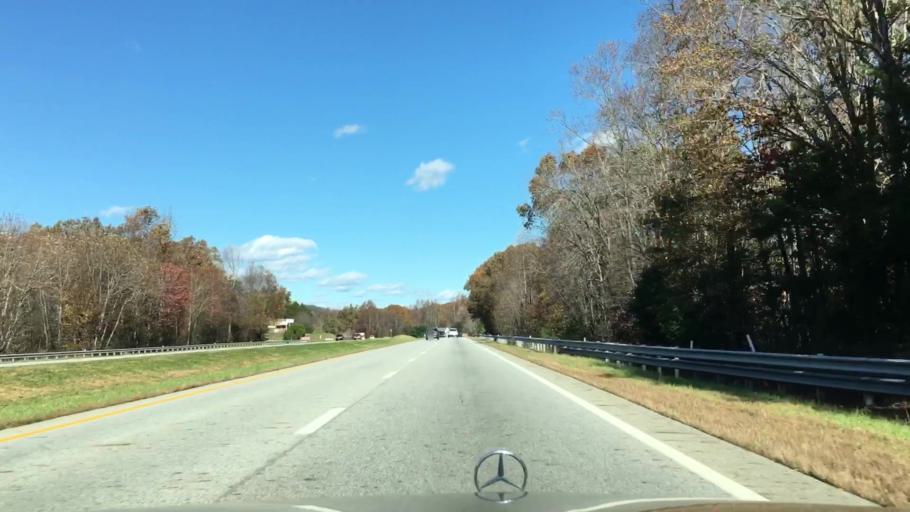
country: US
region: Virginia
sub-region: Nelson County
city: Lovingston
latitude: 37.6839
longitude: -78.9477
